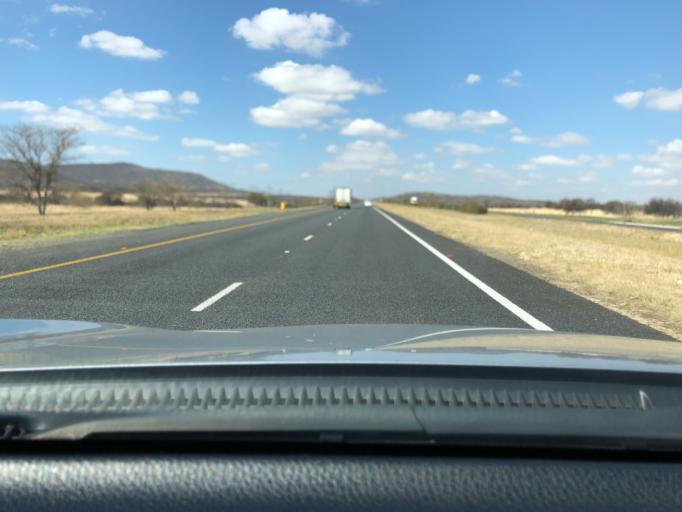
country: ZA
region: KwaZulu-Natal
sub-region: uThukela District Municipality
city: Estcourt
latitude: -28.8118
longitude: 29.6937
